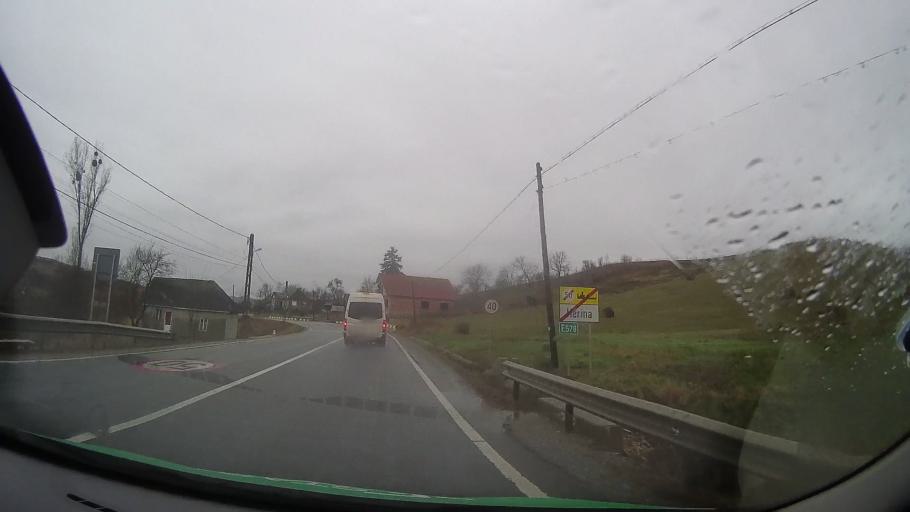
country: RO
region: Bistrita-Nasaud
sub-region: Comuna Galatii Bistritei
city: Galatii Bistritei
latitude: 47.0143
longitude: 24.4083
